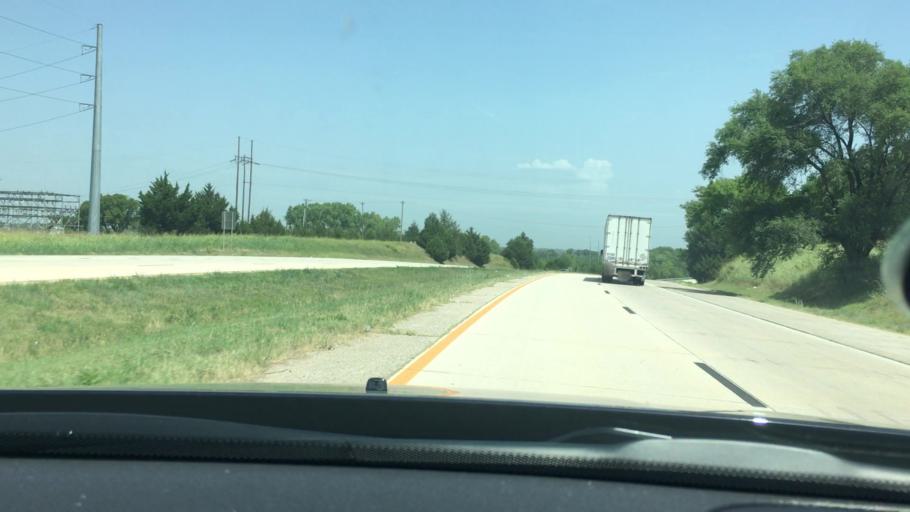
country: US
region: Oklahoma
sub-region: Pontotoc County
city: Ada
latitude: 34.7690
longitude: -96.7049
